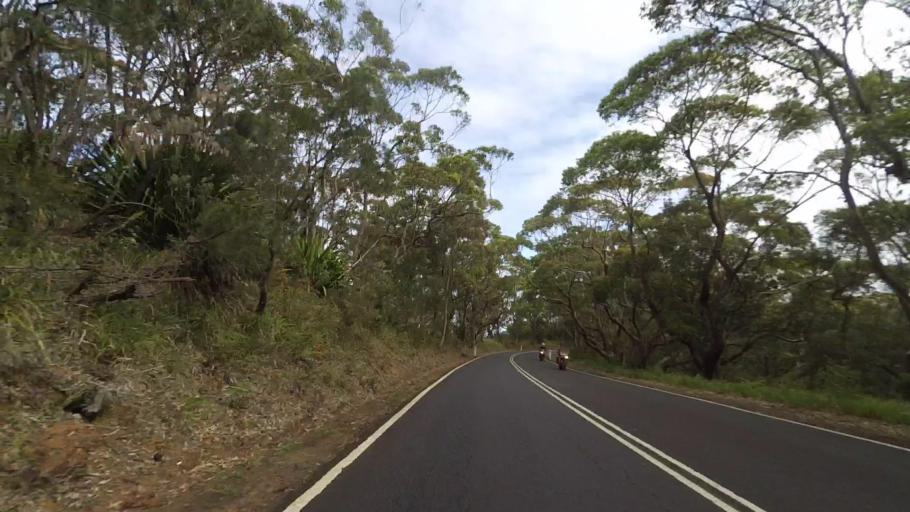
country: AU
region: New South Wales
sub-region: Wollongong
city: Helensburgh
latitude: -34.2197
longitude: 150.9995
